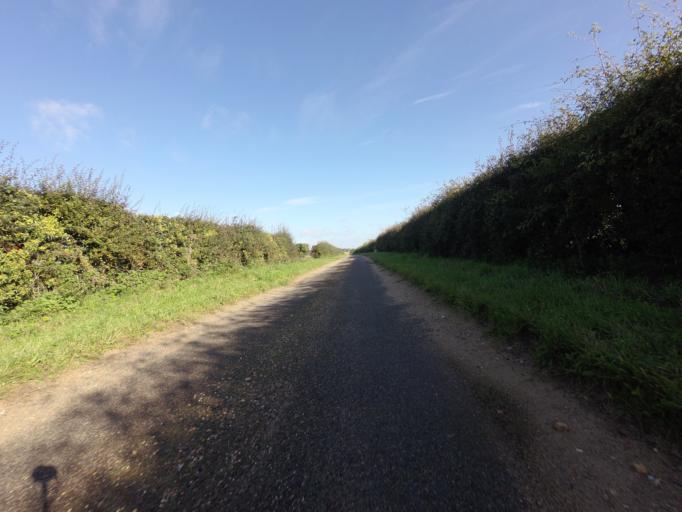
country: GB
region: England
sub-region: Norfolk
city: Dersingham
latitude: 52.8322
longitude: 0.6747
